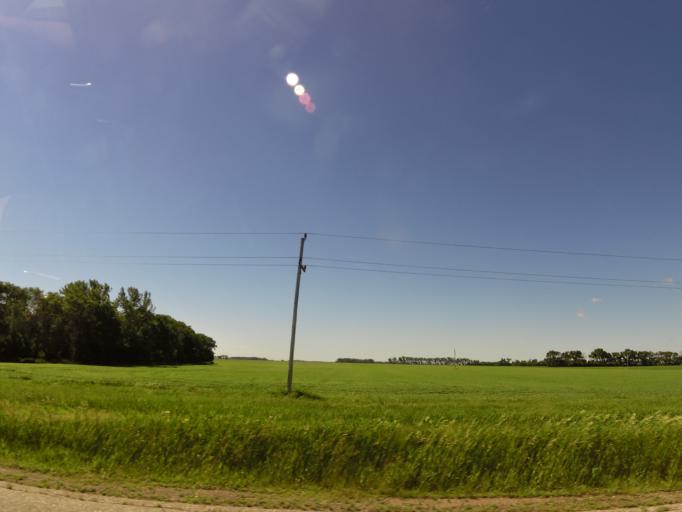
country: US
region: Minnesota
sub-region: Polk County
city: Crookston
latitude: 47.7604
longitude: -96.4910
